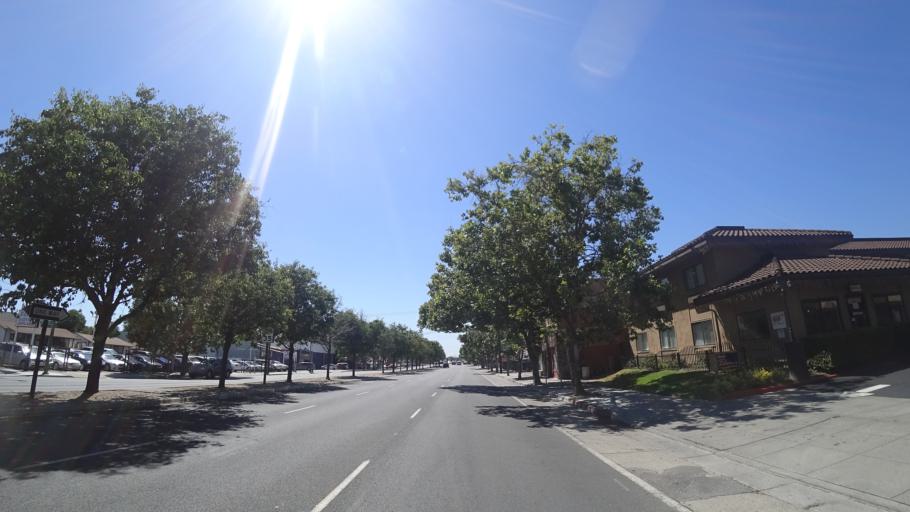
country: US
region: California
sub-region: Santa Clara County
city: San Jose
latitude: 37.3184
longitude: -121.8761
